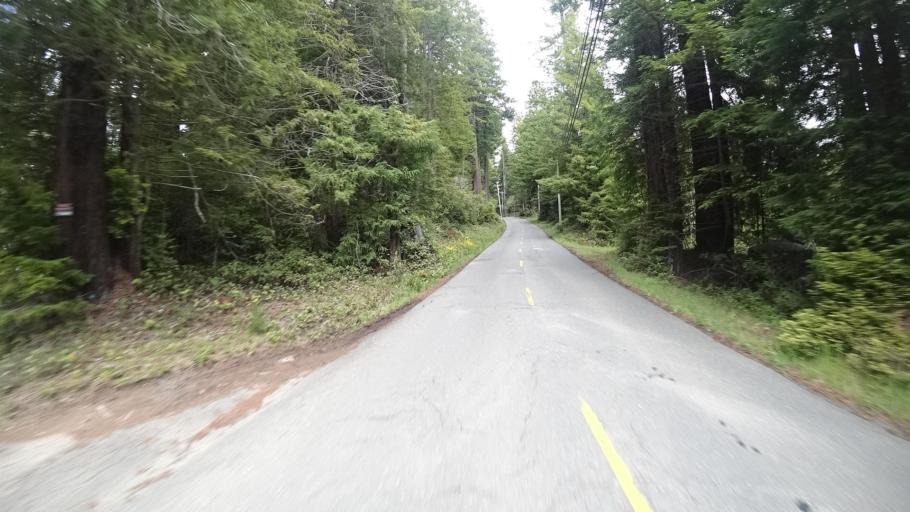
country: US
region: California
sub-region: Humboldt County
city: Bayside
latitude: 40.7903
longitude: -124.0557
